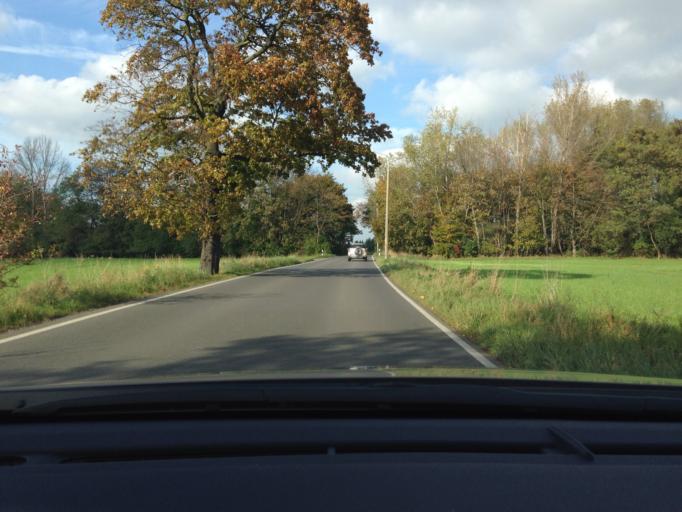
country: DE
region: Saxony
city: Taucha
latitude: 51.3703
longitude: 12.4405
